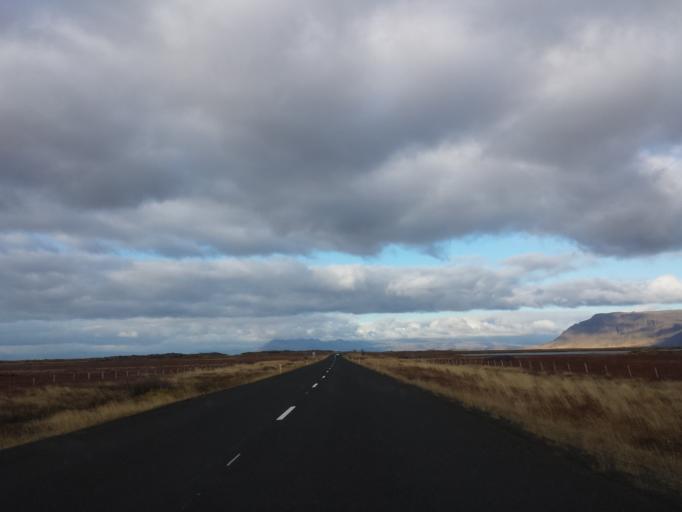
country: IS
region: West
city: Borgarnes
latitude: 64.6839
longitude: -22.0867
